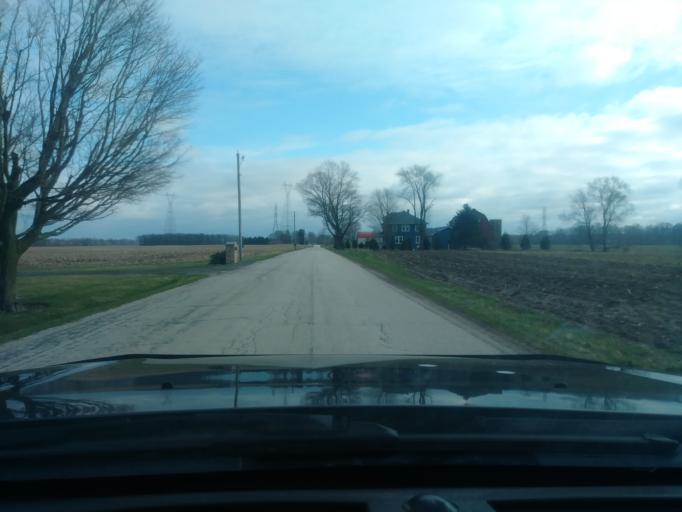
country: US
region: Indiana
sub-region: LaPorte County
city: LaPorte
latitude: 41.5537
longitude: -86.7986
